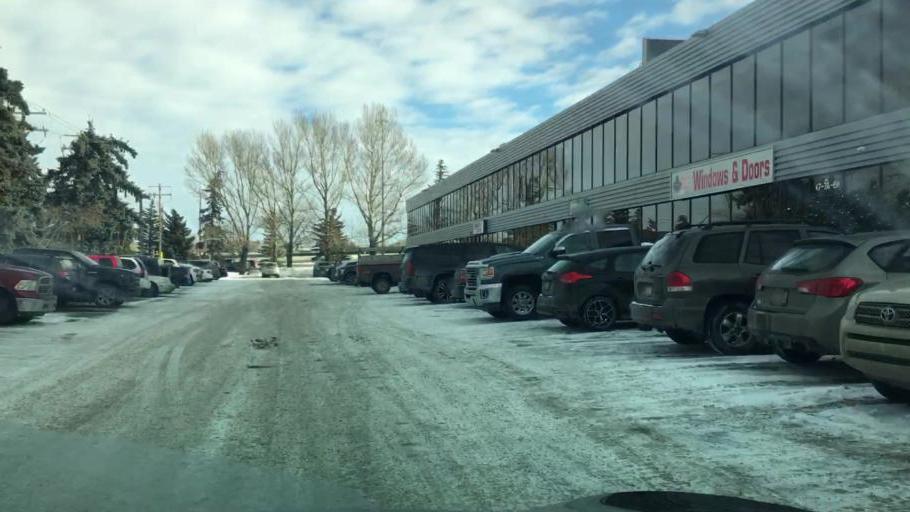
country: CA
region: Alberta
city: Calgary
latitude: 50.9953
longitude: -114.0381
